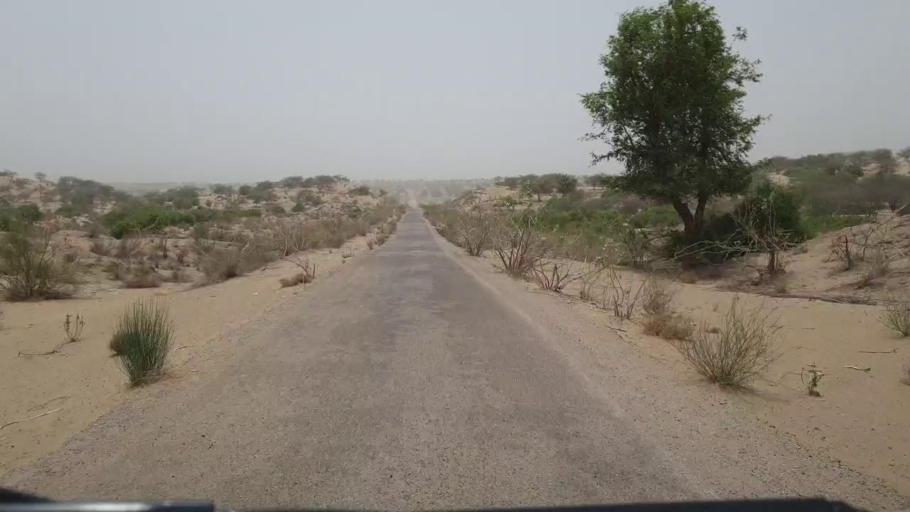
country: PK
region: Sindh
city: Naukot
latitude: 24.7615
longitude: 69.5473
